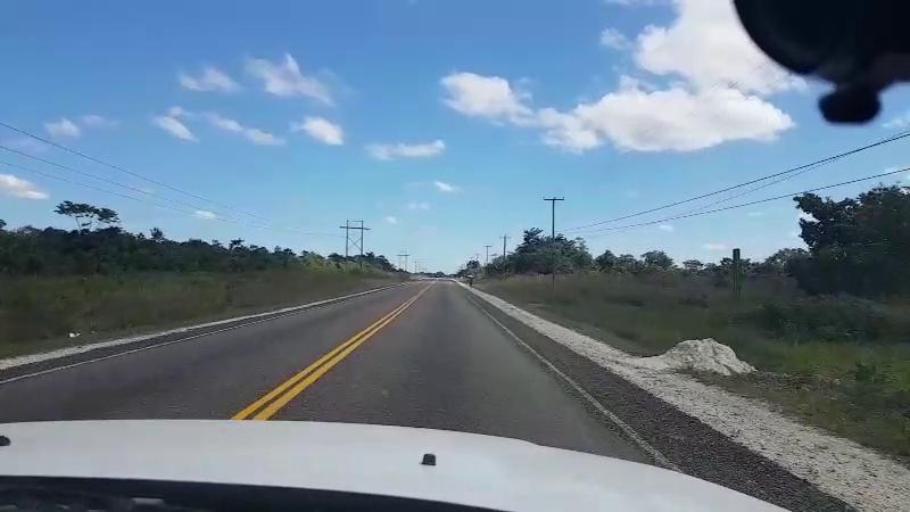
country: BZ
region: Cayo
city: Belmopan
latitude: 17.2771
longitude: -88.6519
